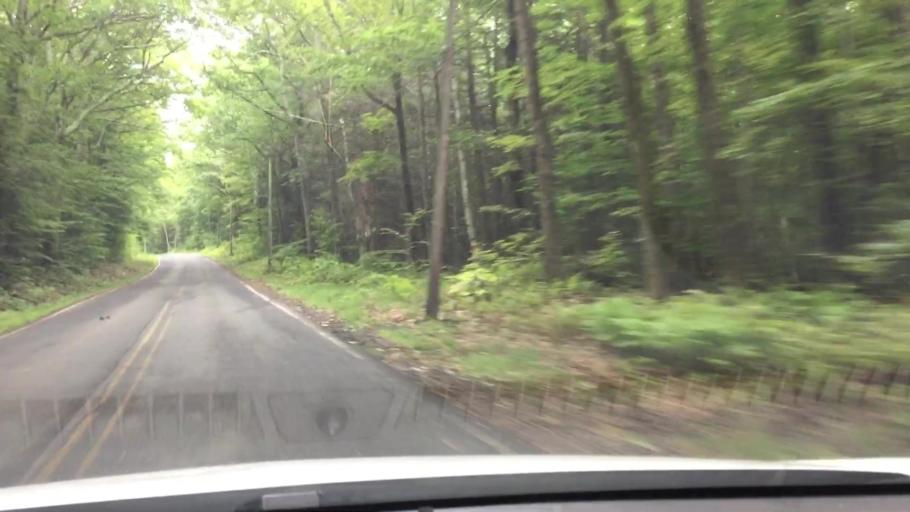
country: US
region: Massachusetts
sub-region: Berkshire County
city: Otis
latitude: 42.2482
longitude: -72.9902
